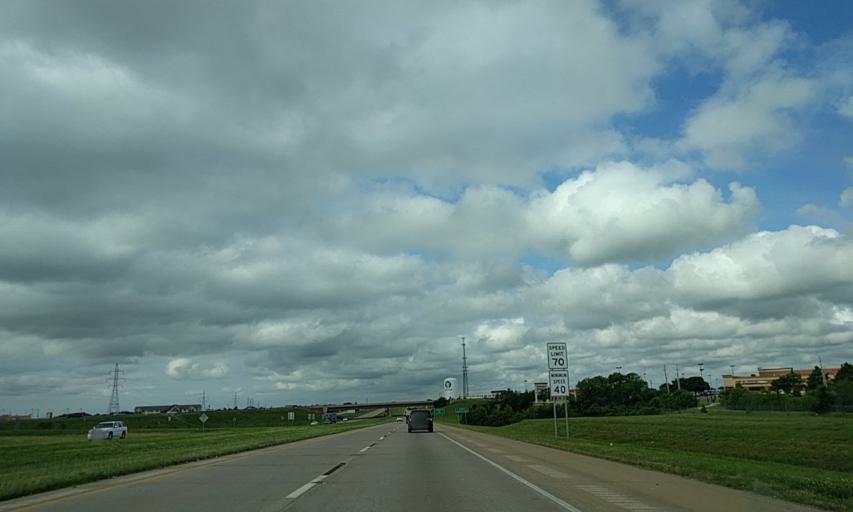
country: US
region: Oklahoma
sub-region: Tulsa County
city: Owasso
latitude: 36.2955
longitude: -95.8308
